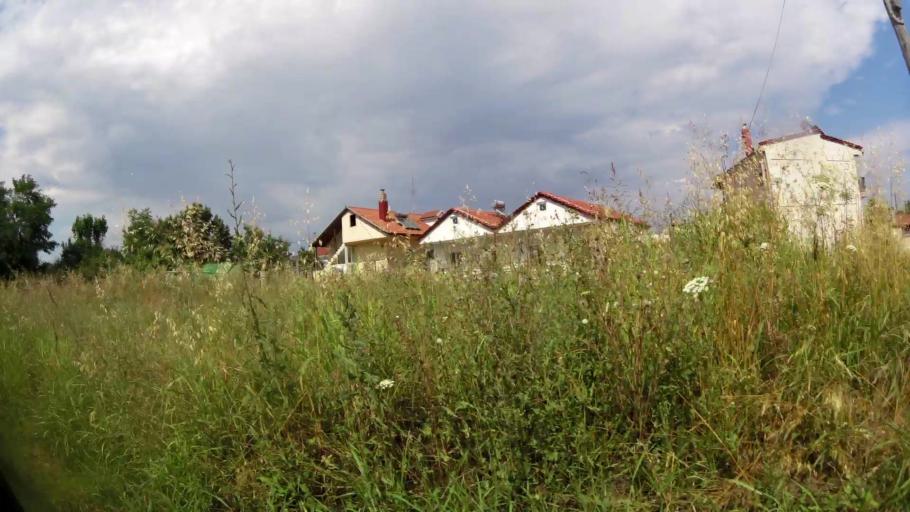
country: GR
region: Central Macedonia
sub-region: Nomos Pierias
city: Makrygialos
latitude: 40.4115
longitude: 22.6048
